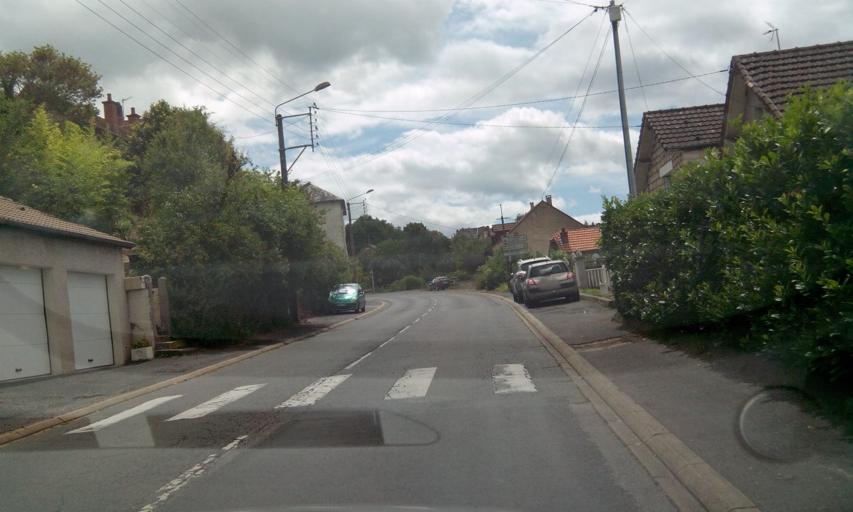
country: FR
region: Limousin
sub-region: Departement de la Correze
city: Brive-la-Gaillarde
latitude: 45.1496
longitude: 1.5436
